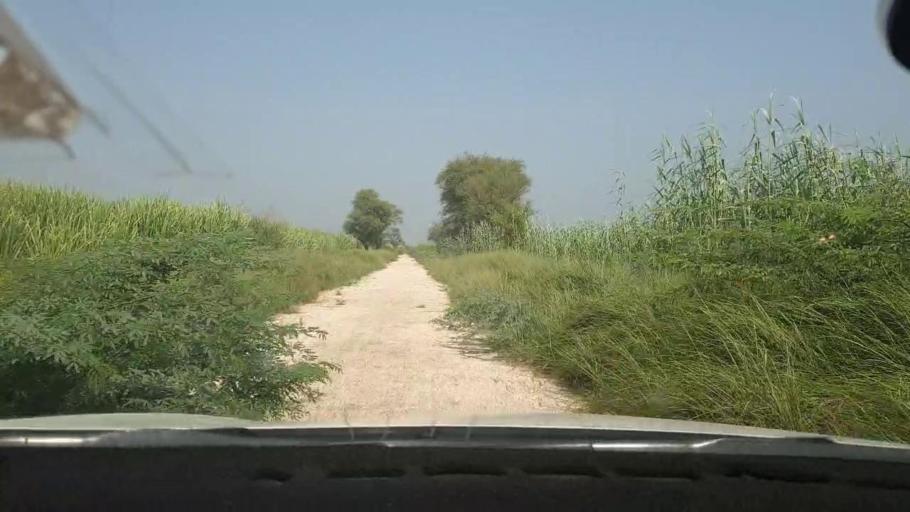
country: PK
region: Sindh
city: Tando Mittha Khan
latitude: 25.9293
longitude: 69.2198
